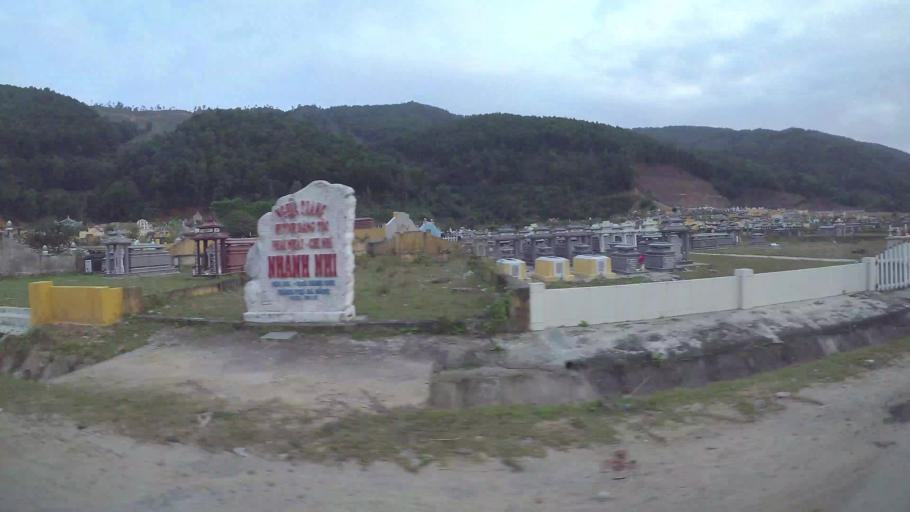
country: VN
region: Da Nang
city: Lien Chieu
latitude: 16.0566
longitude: 108.1262
